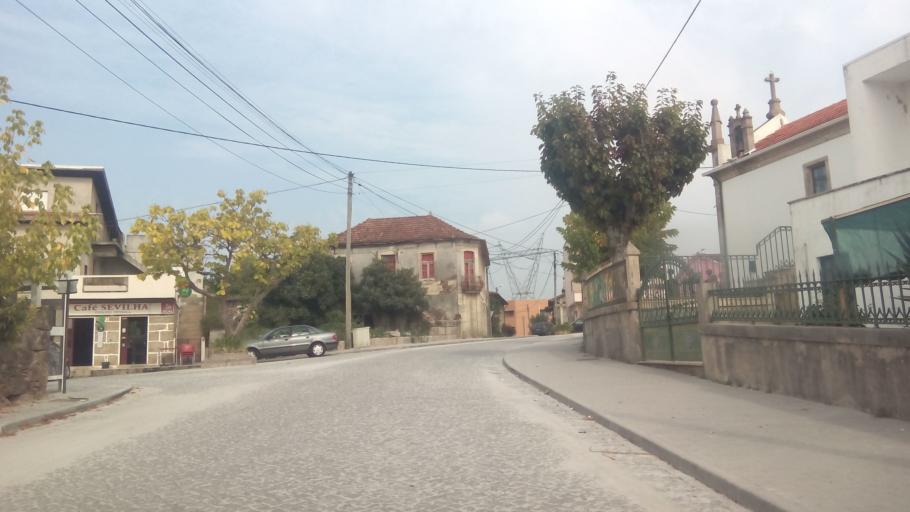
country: PT
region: Porto
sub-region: Paredes
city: Gandra
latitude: 41.1839
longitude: -8.4422
